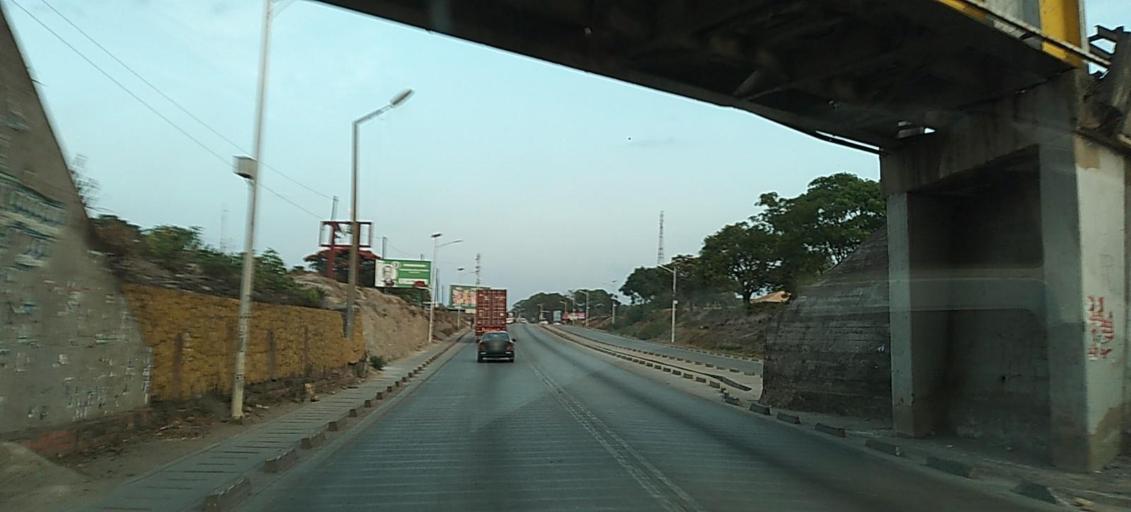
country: ZM
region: Copperbelt
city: Chingola
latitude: -12.5465
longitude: 27.8542
